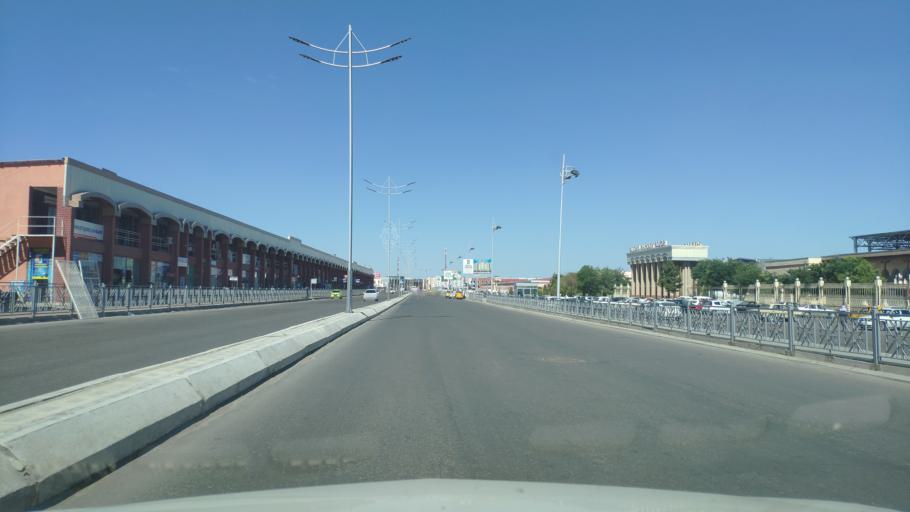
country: UZ
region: Bukhara
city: Bukhara
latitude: 39.7799
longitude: 64.3990
